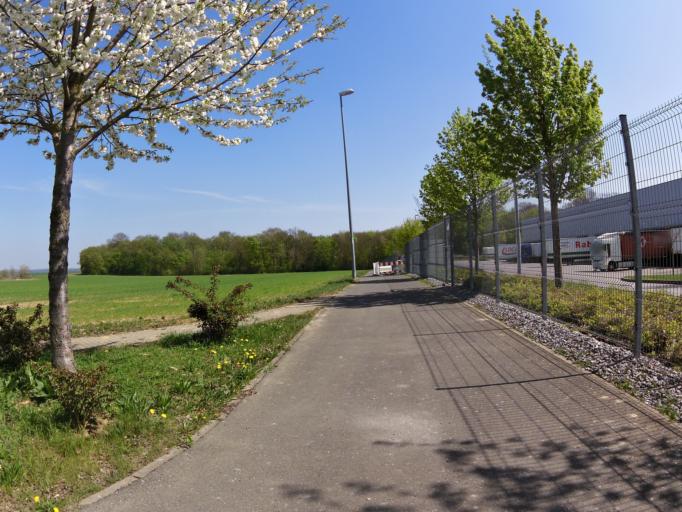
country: DE
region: Bavaria
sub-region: Regierungsbezirk Unterfranken
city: Giebelstadt
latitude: 49.6911
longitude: 9.9443
